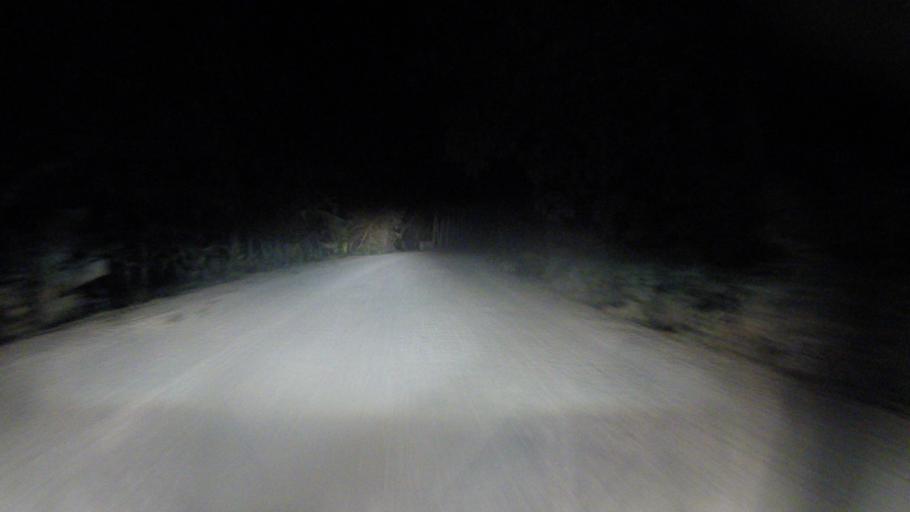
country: TL
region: Viqueque
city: Viqueque
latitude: -8.8325
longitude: 126.5207
